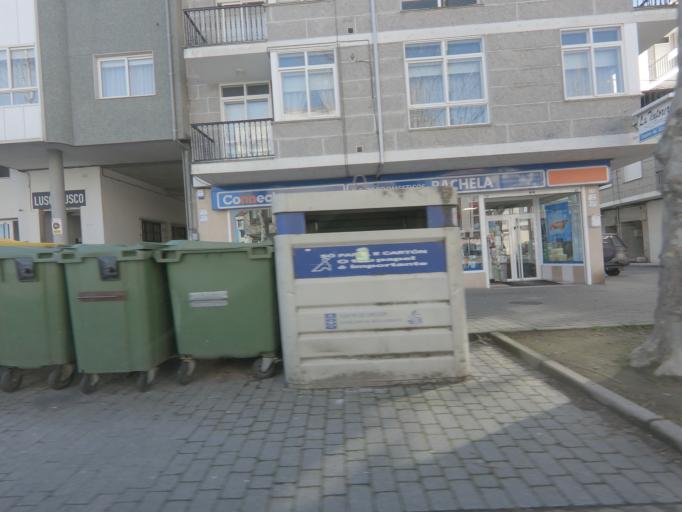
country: ES
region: Galicia
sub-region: Provincia de Ourense
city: Allariz
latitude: 42.1870
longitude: -7.7981
